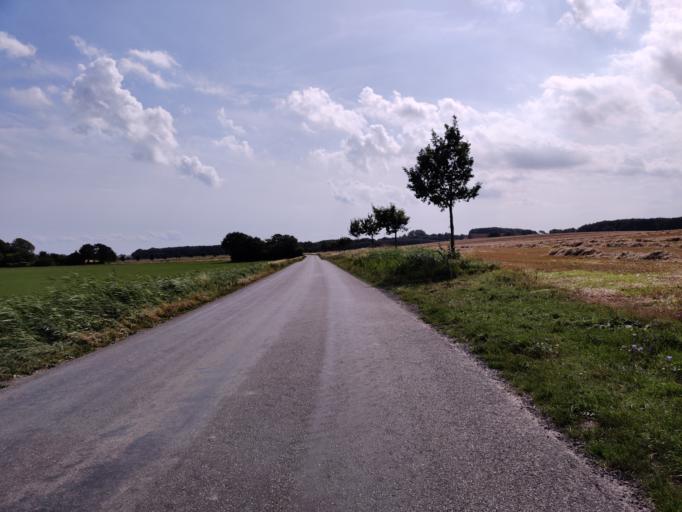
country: DK
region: Zealand
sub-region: Guldborgsund Kommune
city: Nykobing Falster
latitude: 54.6563
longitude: 11.8877
